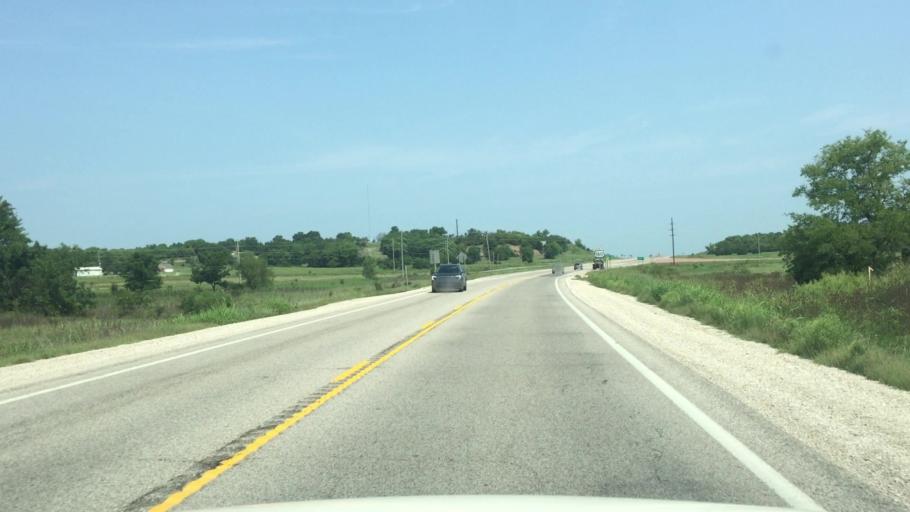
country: US
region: Kansas
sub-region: Montgomery County
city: Cherryvale
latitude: 37.2051
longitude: -95.5846
